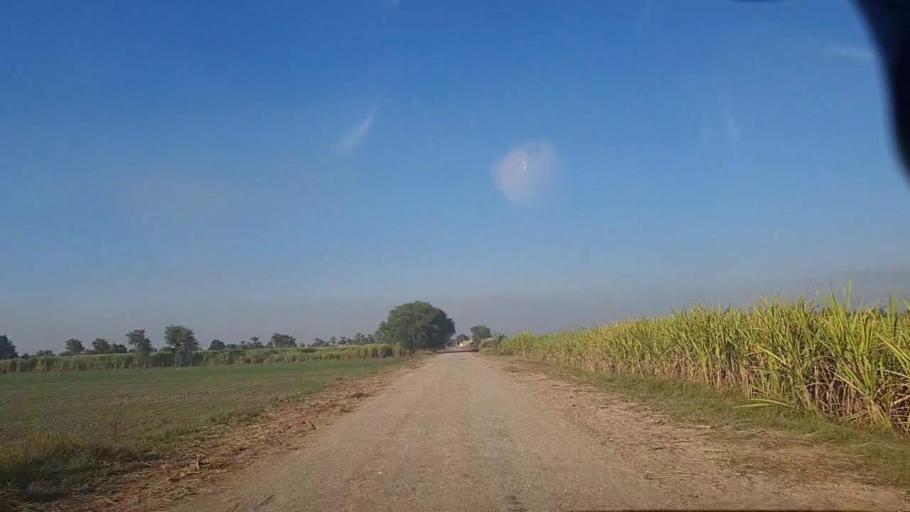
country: PK
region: Sindh
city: Sobhadero
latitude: 27.4133
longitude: 68.4227
